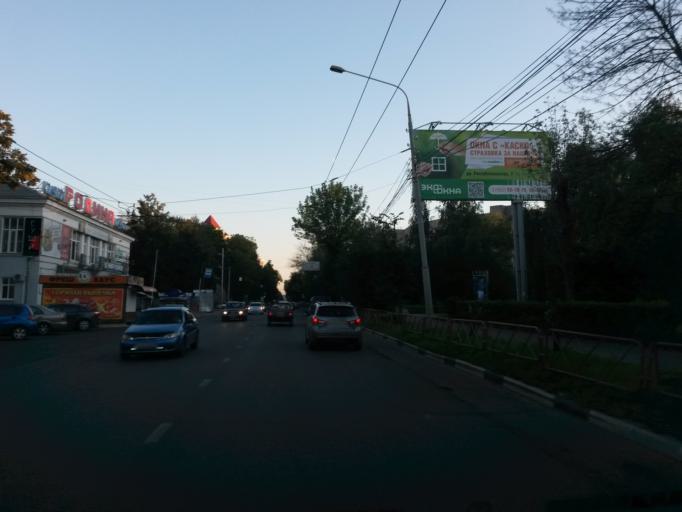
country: RU
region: Jaroslavl
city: Yaroslavl
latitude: 57.6371
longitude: 39.8821
